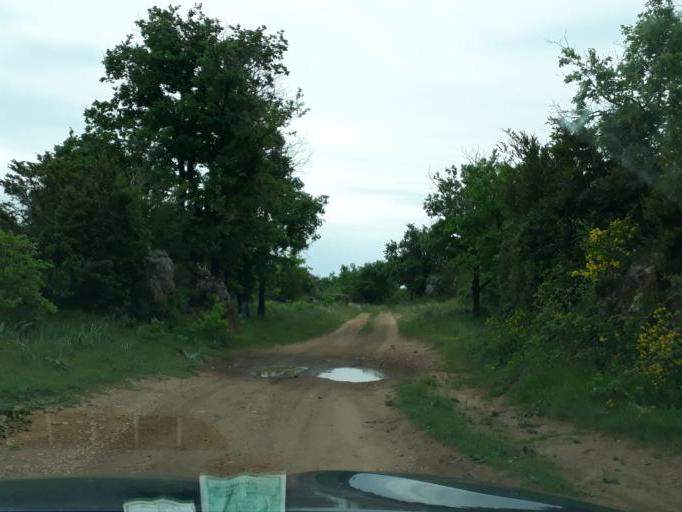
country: FR
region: Languedoc-Roussillon
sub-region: Departement de l'Herault
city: Lodeve
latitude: 43.8158
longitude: 3.2798
